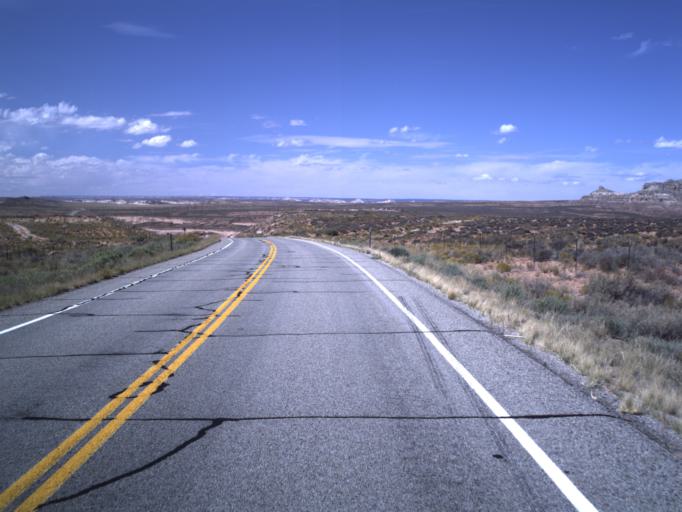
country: US
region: Utah
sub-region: San Juan County
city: Blanding
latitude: 37.3014
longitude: -109.4420
